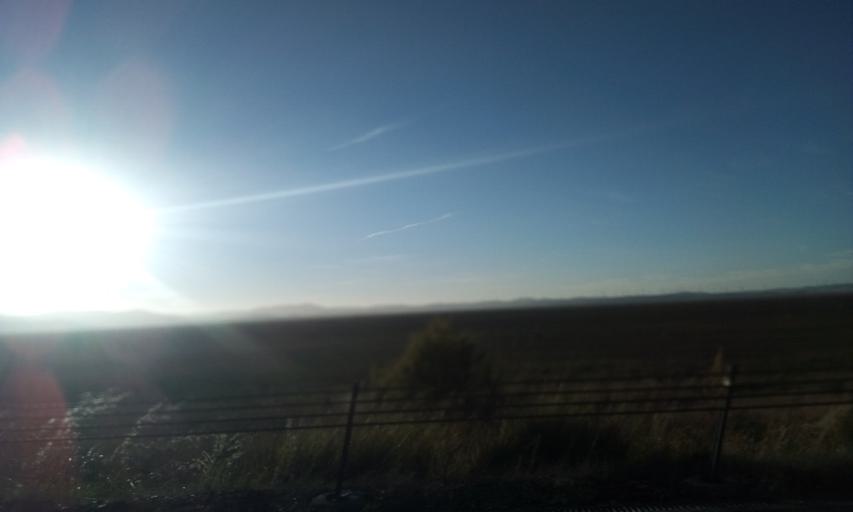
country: AU
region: New South Wales
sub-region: Yass Valley
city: Gundaroo
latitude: -35.0504
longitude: 149.3758
